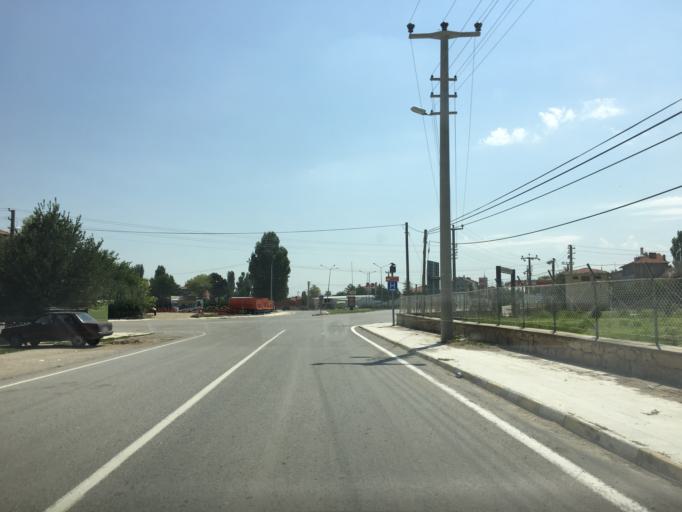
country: TR
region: Eskisehir
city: Cifteler
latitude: 39.3697
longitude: 31.0345
